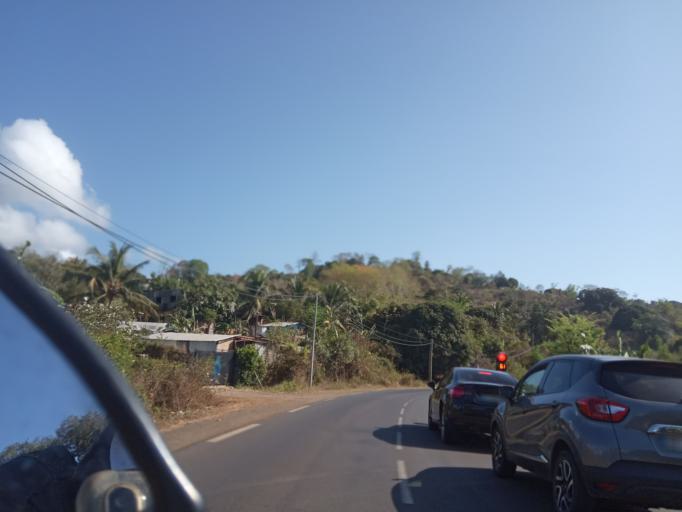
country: YT
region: Bandrele
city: Bandrele
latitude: -12.9186
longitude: 45.1840
